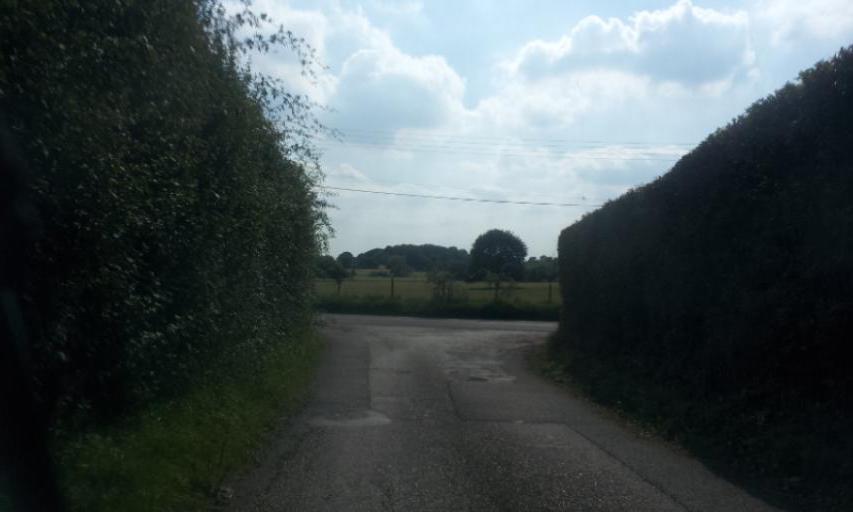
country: GB
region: England
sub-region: Kent
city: Marden
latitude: 51.2138
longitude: 0.4910
